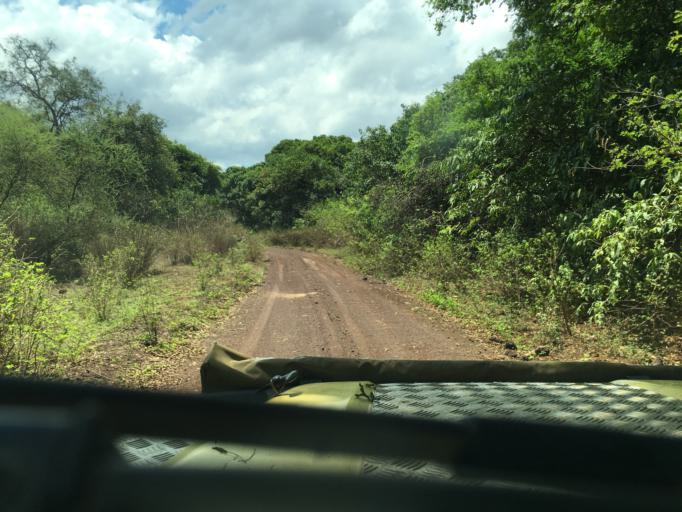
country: TZ
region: Arusha
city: Mto wa Mbu
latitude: -3.4159
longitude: 35.8192
